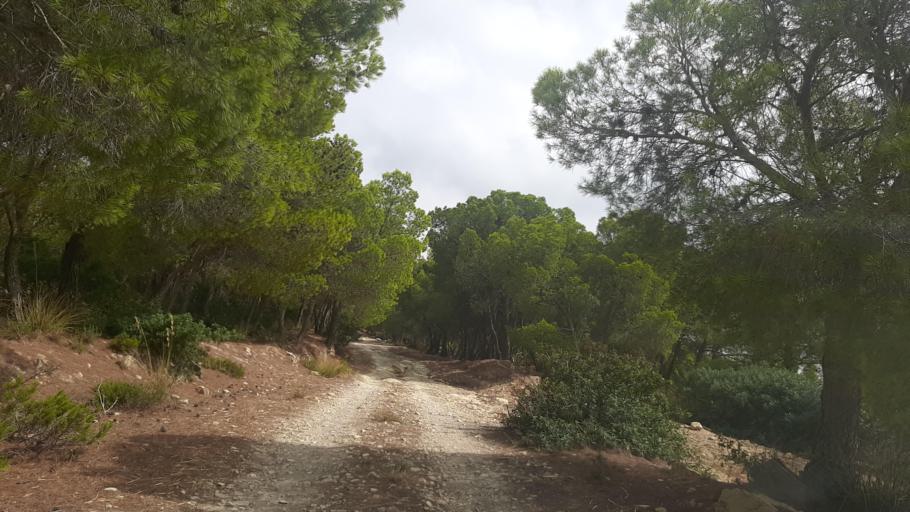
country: TN
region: Zaghwan
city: El Fahs
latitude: 36.1963
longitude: 9.8432
